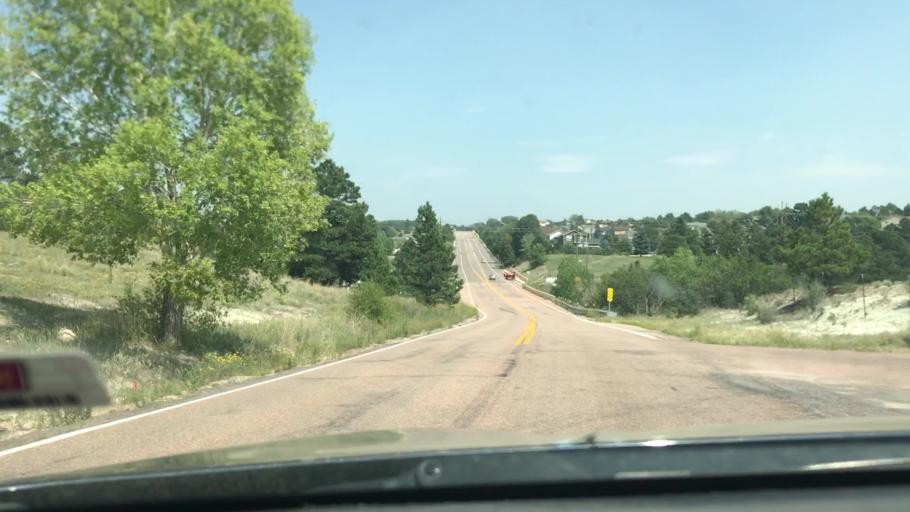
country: US
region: Colorado
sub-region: El Paso County
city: Gleneagle
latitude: 38.9807
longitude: -104.7870
